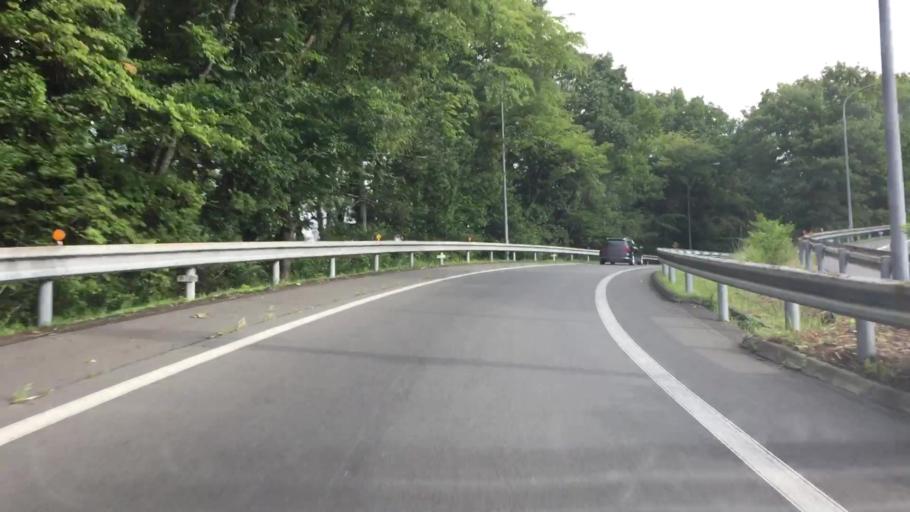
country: JP
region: Tochigi
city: Imaichi
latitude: 36.6878
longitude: 139.7569
